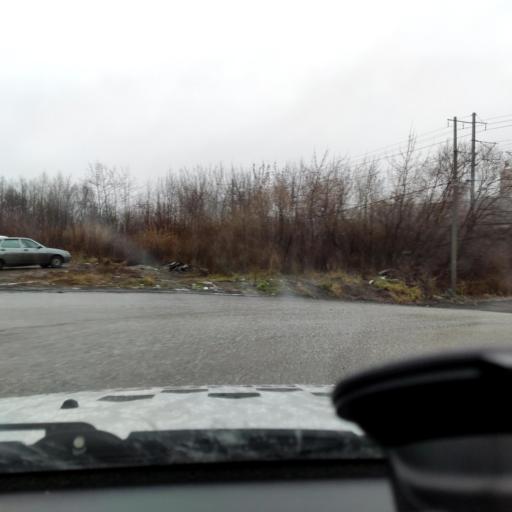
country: RU
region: Perm
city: Perm
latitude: 58.0590
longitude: 56.3270
